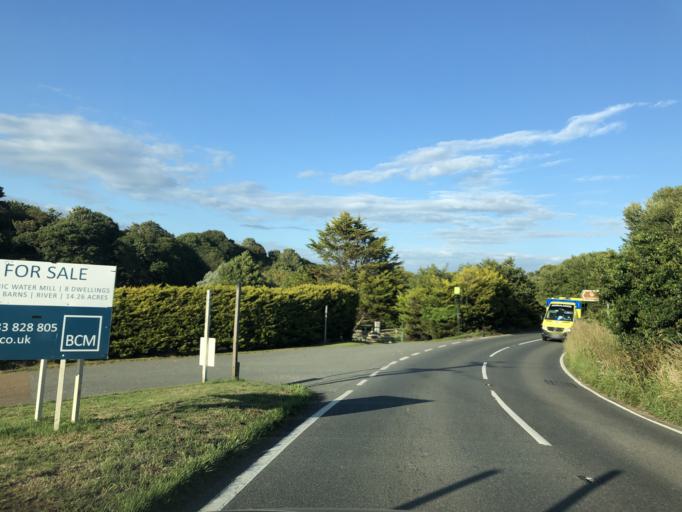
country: GB
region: England
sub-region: Isle of Wight
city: Shalfleet
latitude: 50.6790
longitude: -1.4148
